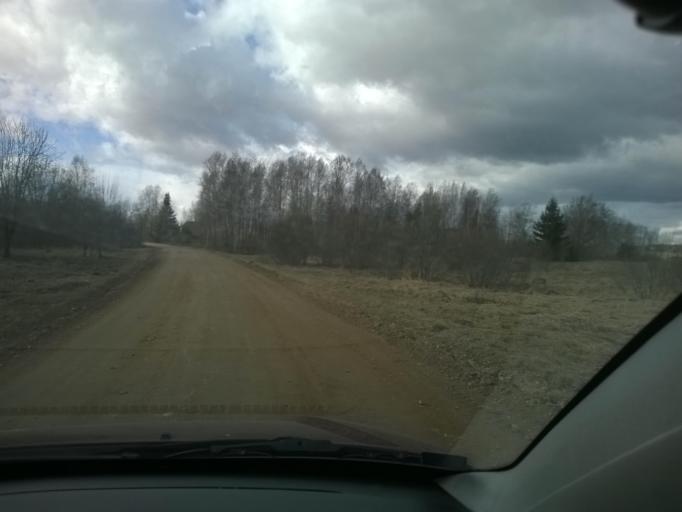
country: EE
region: Tartu
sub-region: Alatskivi vald
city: Kallaste
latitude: 58.3829
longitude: 27.0523
